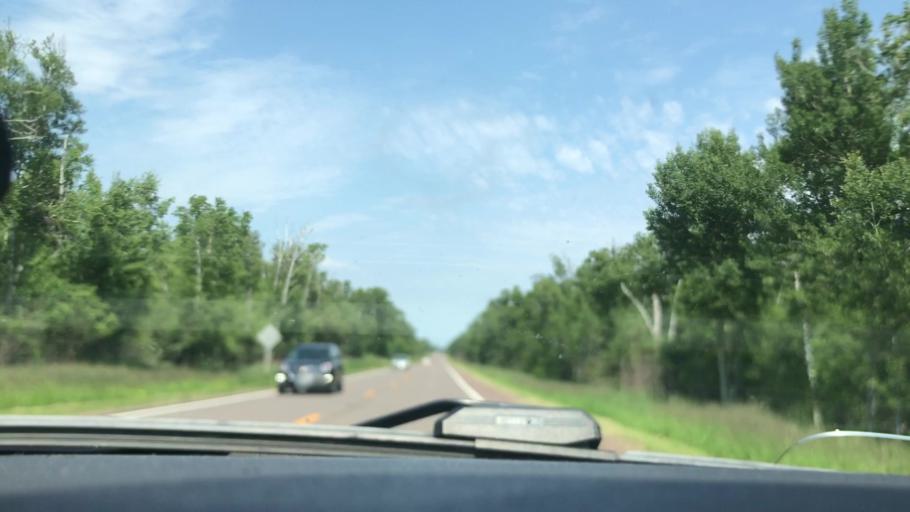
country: US
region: Minnesota
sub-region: Lake County
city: Silver Bay
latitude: 47.5010
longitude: -90.9664
